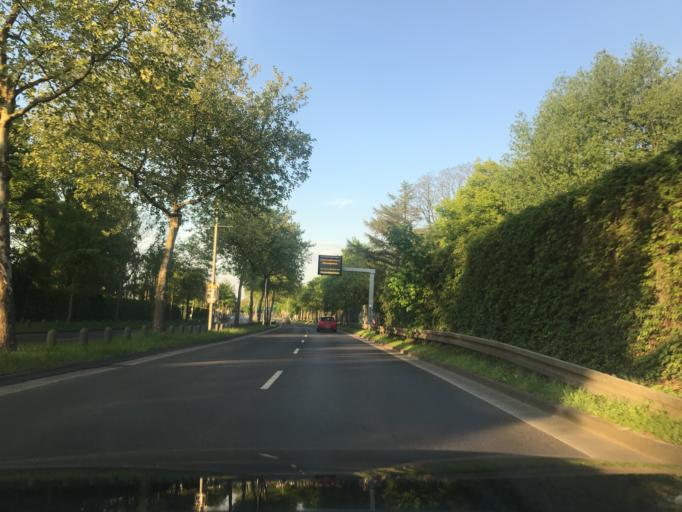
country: DE
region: North Rhine-Westphalia
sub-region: Regierungsbezirk Dusseldorf
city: Monchengladbach
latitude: 51.1673
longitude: 6.3839
